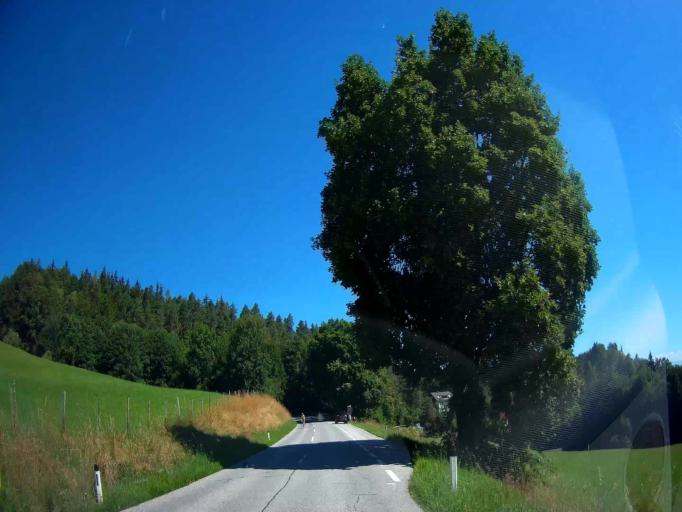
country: AT
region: Carinthia
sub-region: Politischer Bezirk Klagenfurt Land
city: Maria Worth
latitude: 46.5968
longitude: 14.1581
